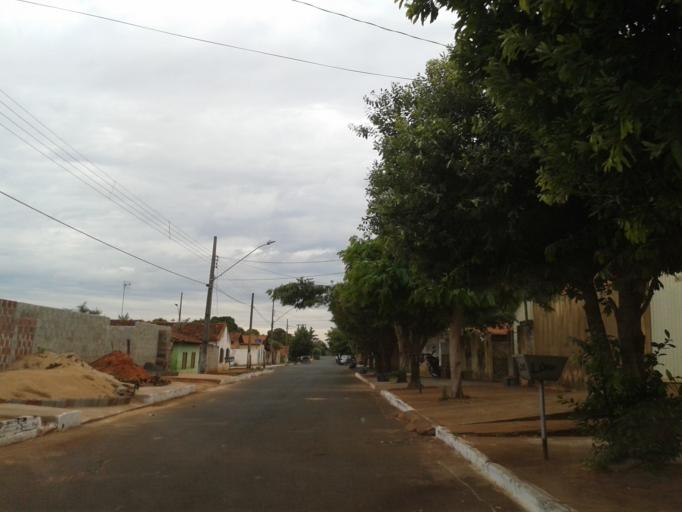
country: BR
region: Minas Gerais
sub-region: Santa Vitoria
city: Santa Vitoria
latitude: -18.8406
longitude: -50.1293
